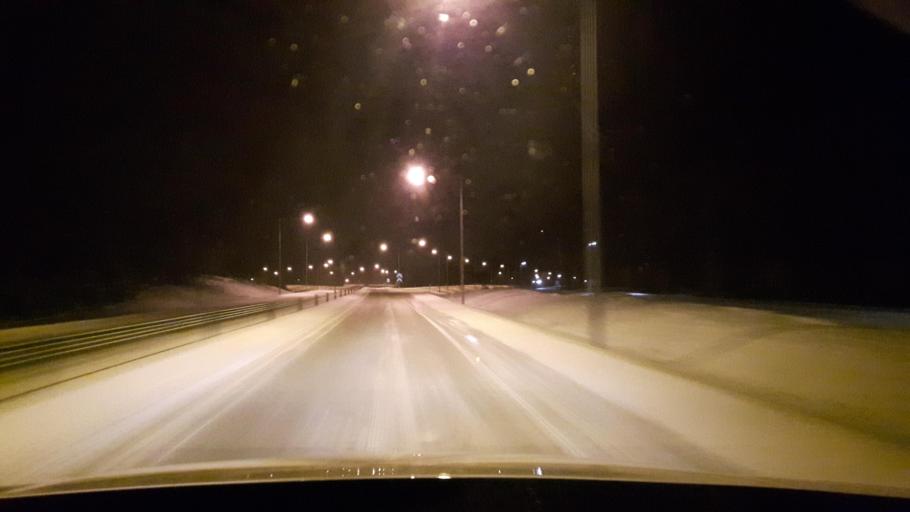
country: SE
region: Vaesterbotten
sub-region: Umea Kommun
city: Saevar
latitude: 63.8902
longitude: 20.5189
